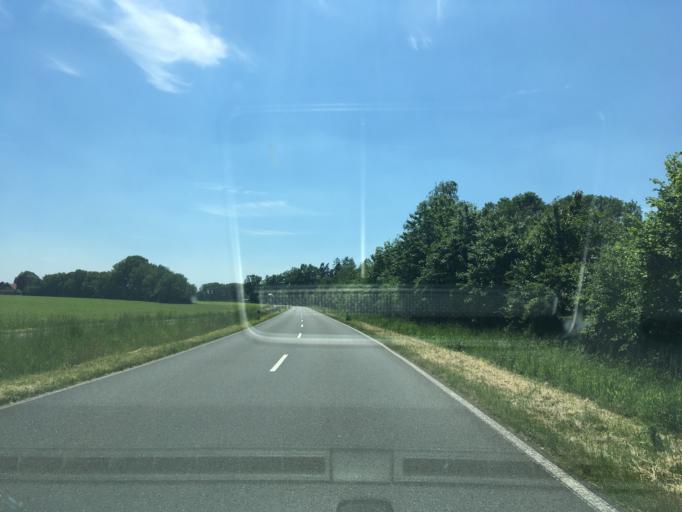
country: DE
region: North Rhine-Westphalia
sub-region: Regierungsbezirk Munster
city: Borken
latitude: 51.8774
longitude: 6.8281
